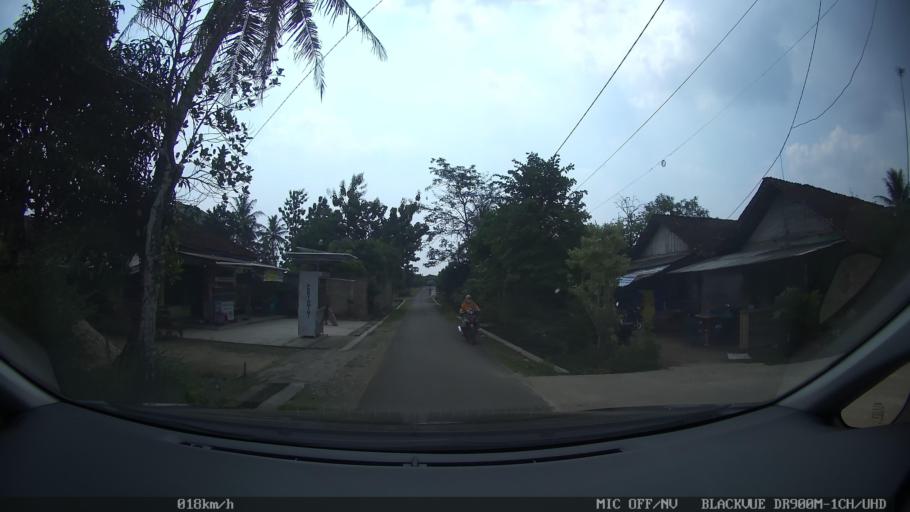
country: ID
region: Lampung
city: Gadingrejo
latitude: -5.3691
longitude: 105.0648
